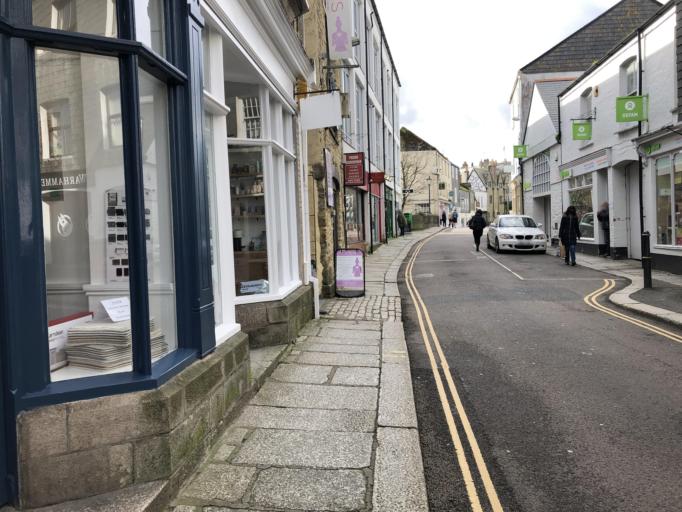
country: GB
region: England
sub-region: Cornwall
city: Truro
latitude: 50.2641
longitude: -5.0484
